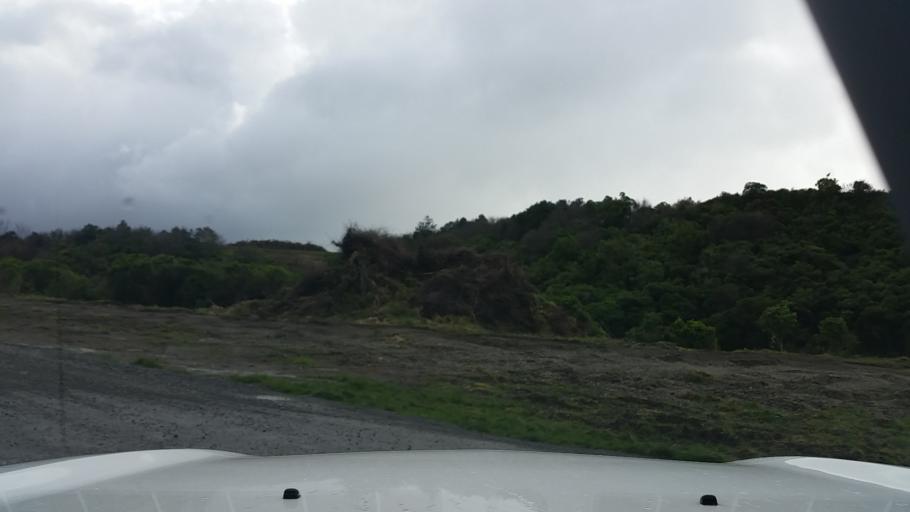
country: NZ
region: Wellington
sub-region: Upper Hutt City
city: Upper Hutt
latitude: -41.3672
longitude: 175.1867
